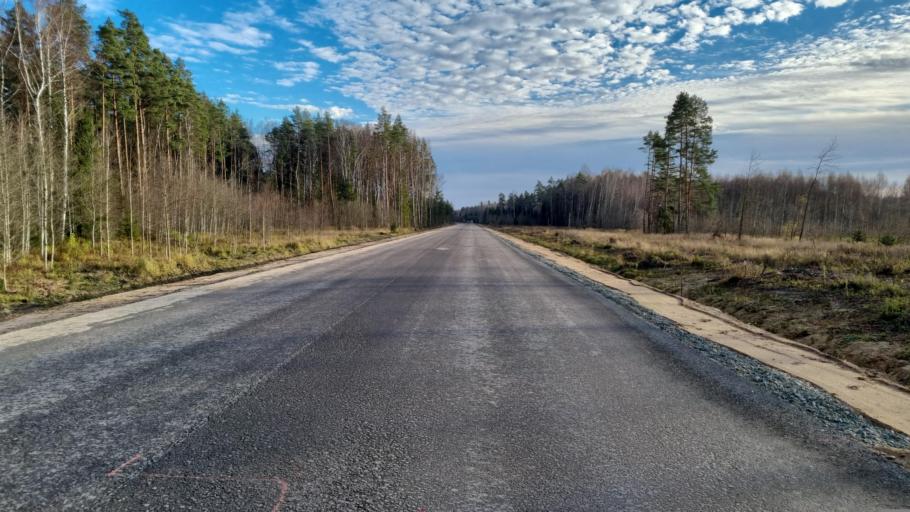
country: LV
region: Kekava
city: Kekava
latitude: 56.7998
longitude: 24.2053
